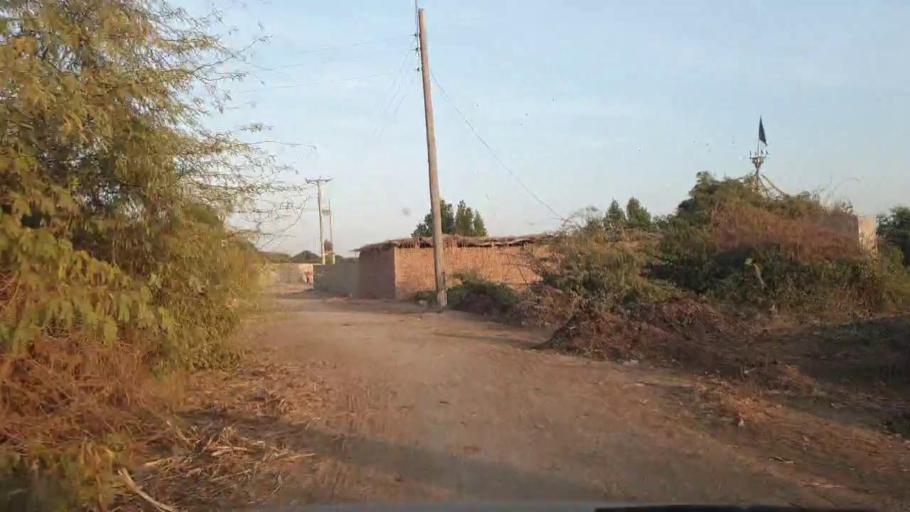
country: PK
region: Sindh
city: Chambar
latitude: 25.2789
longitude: 68.8361
